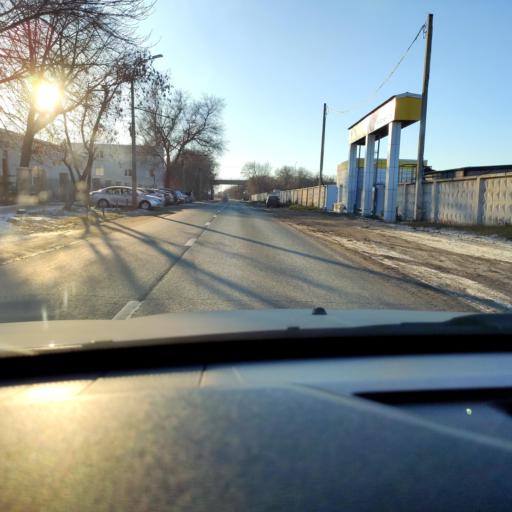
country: RU
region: Samara
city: Samara
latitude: 53.1162
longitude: 50.0664
